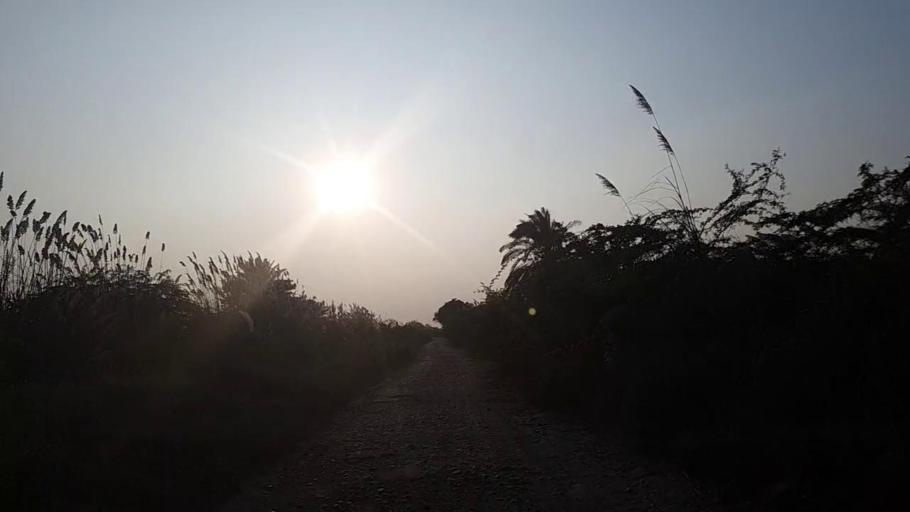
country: PK
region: Sindh
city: Mirpur Sakro
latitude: 24.5569
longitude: 67.5834
